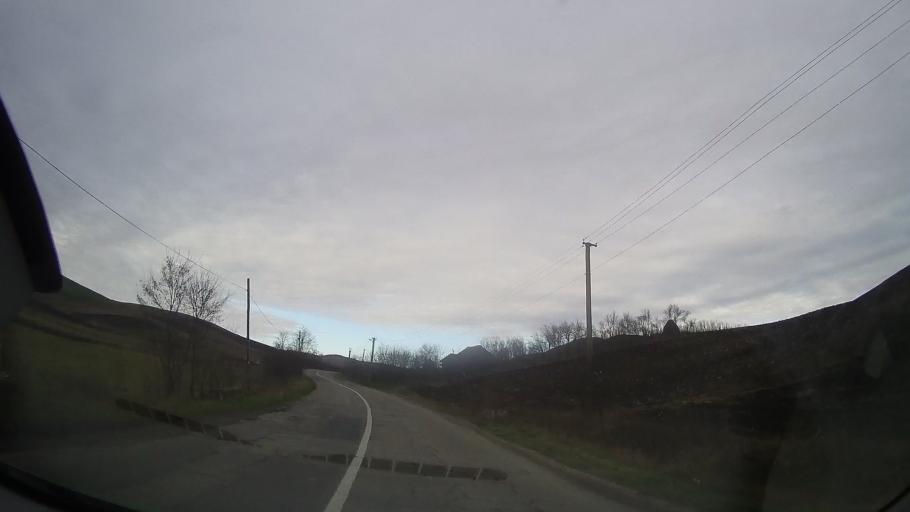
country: RO
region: Cluj
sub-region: Comuna Camarasu
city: Camarasu
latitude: 46.8066
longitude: 24.1453
